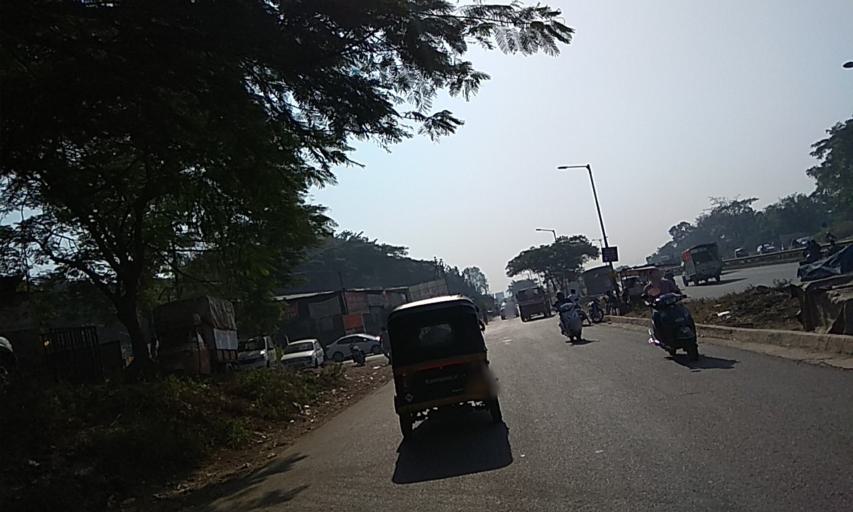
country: IN
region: Maharashtra
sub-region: Pune Division
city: Kharakvasla
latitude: 18.4737
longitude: 73.8105
